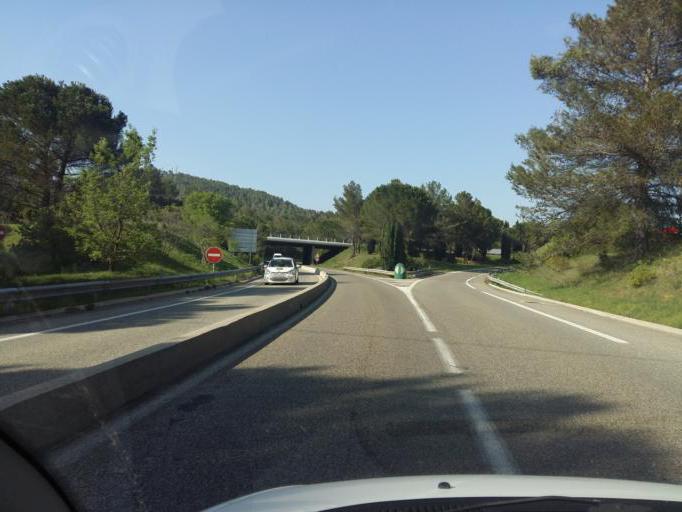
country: FR
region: Provence-Alpes-Cote d'Azur
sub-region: Departement du Var
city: Le Val
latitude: 43.4204
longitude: 6.0663
